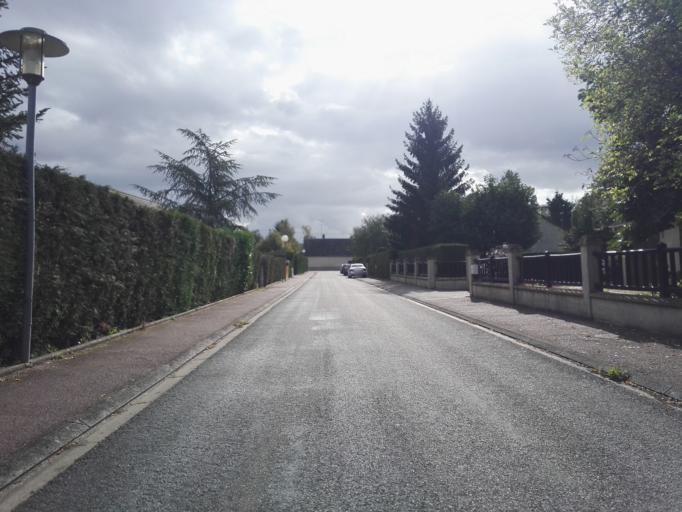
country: FR
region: Haute-Normandie
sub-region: Departement de l'Eure
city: Menilles
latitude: 49.0362
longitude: 1.3568
